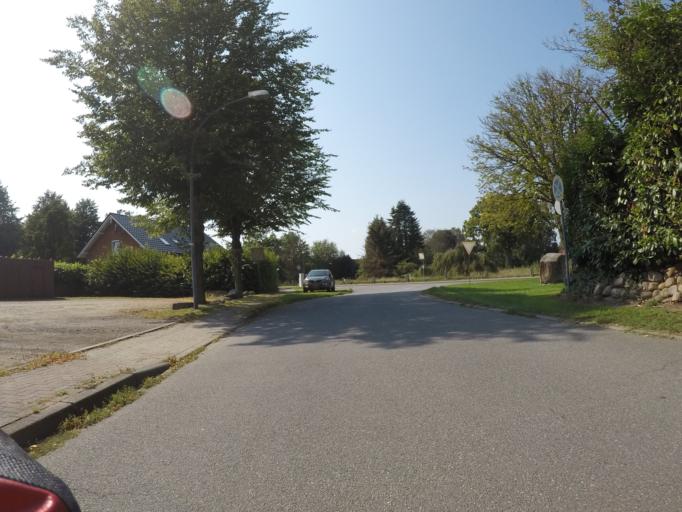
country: DE
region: Schleswig-Holstein
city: Stuvenborn
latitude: 53.8524
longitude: 10.1269
